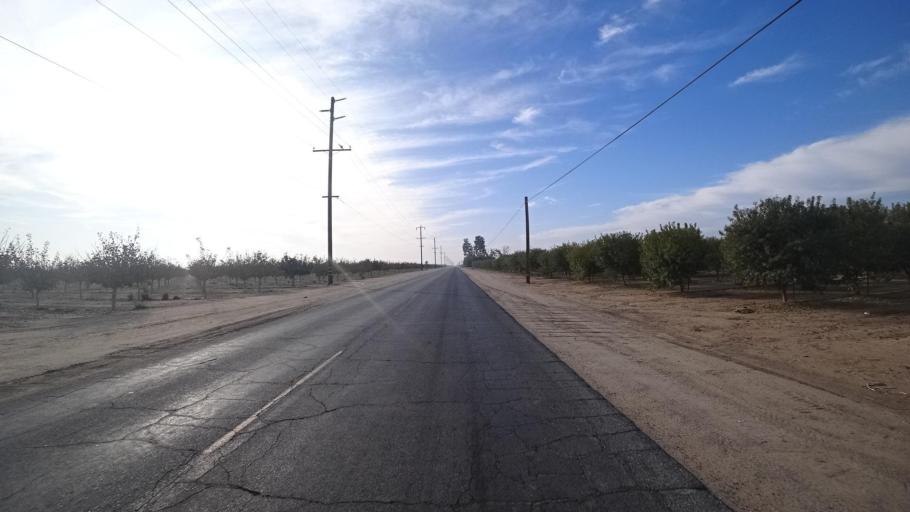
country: US
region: California
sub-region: Kern County
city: Delano
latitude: 35.7600
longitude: -119.2053
